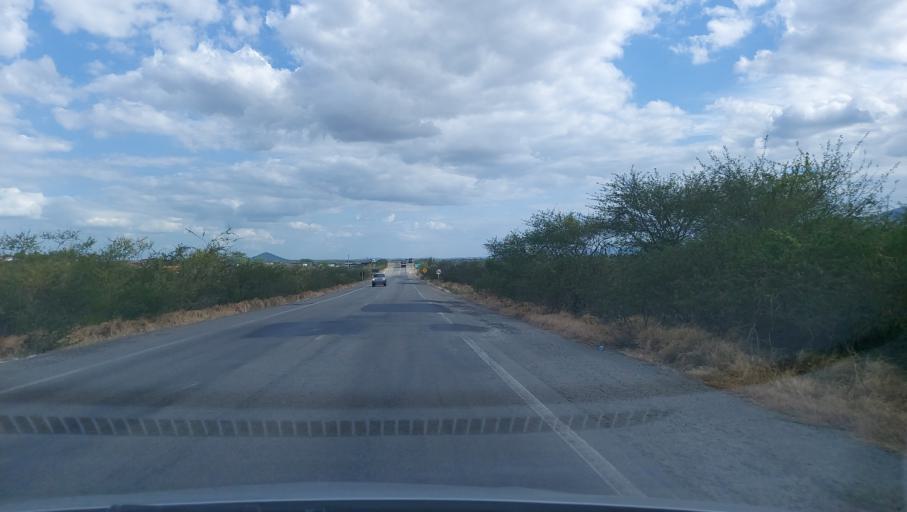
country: BR
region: Bahia
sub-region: Castro Alves
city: Castro Alves
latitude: -12.5784
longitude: -39.5240
